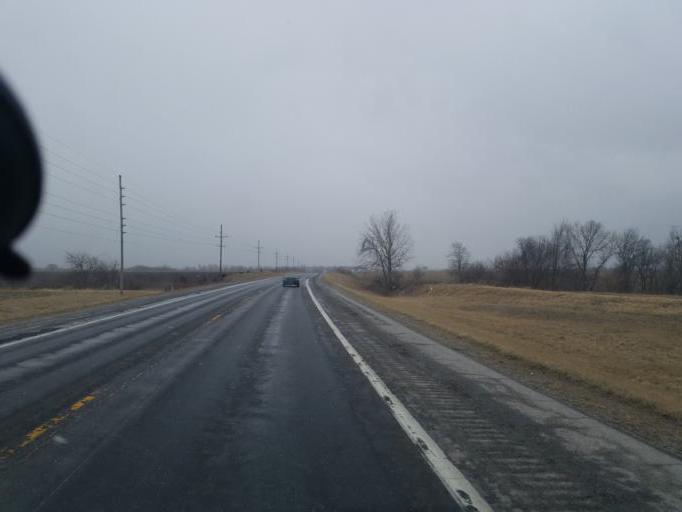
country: US
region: Missouri
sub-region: Schuyler County
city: Lancaster
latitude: 40.3743
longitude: -92.5592
